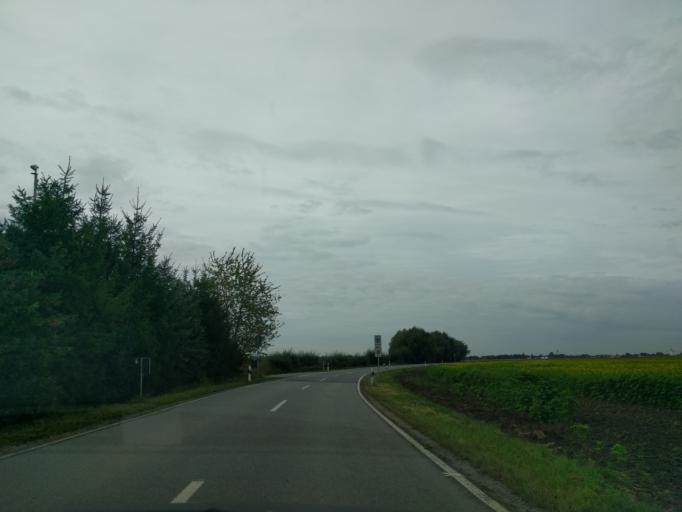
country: DE
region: Bavaria
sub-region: Lower Bavaria
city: Otzing
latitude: 48.7498
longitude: 12.7798
